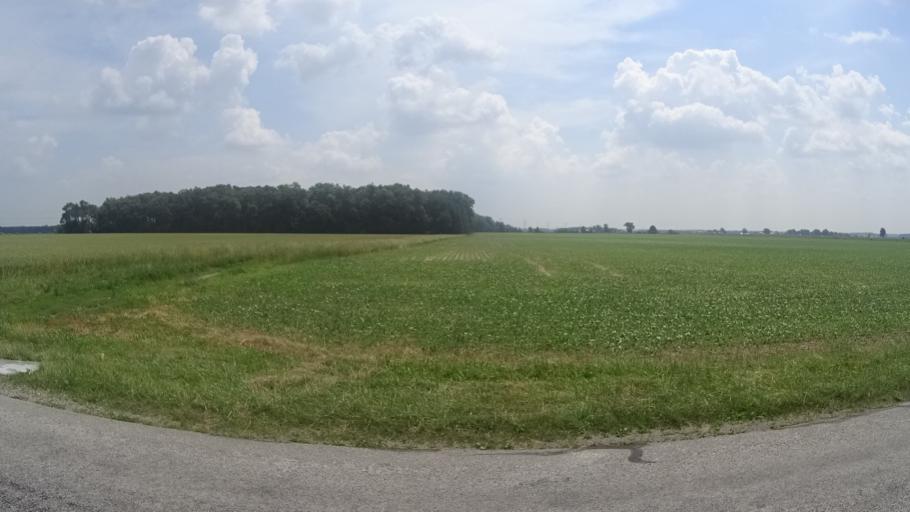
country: US
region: Ohio
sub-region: Huron County
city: Monroeville
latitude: 41.3394
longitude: -82.6938
